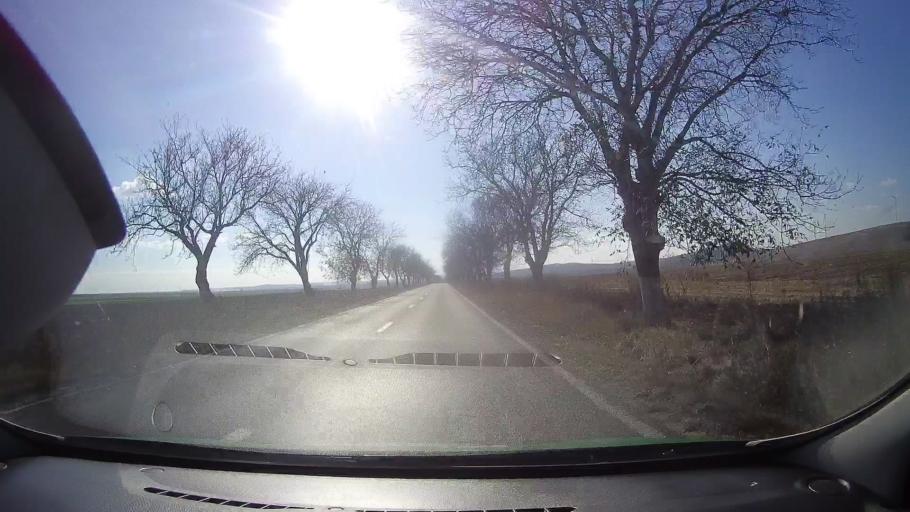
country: RO
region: Tulcea
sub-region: Comuna Ceamurlia de Jos
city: Ceamurlia de Jos
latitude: 44.7895
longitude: 28.6898
